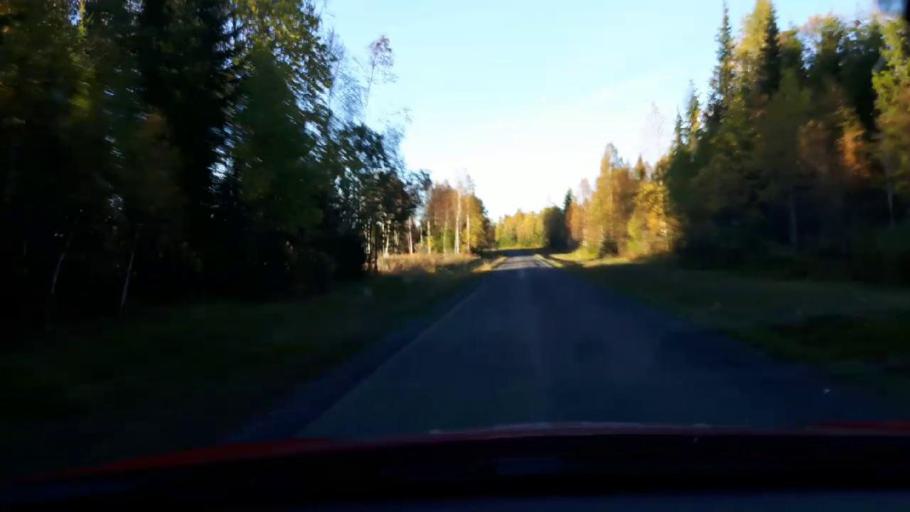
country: SE
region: Jaemtland
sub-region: Krokoms Kommun
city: Krokom
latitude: 63.4264
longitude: 14.6098
